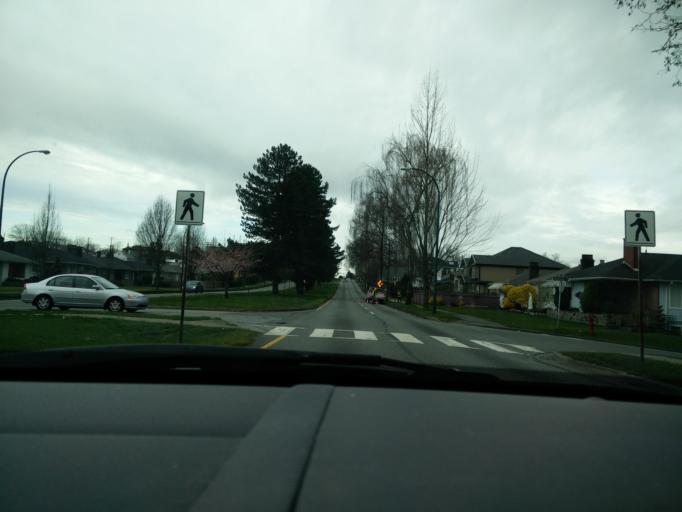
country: CA
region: British Columbia
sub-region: Fraser Valley Regional District
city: North Vancouver
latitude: 49.2696
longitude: -123.0517
